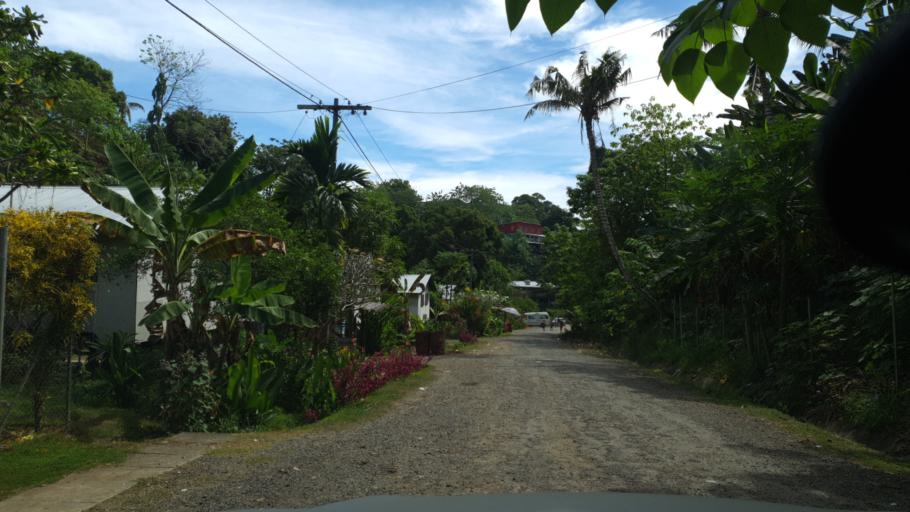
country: SB
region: Guadalcanal
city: Honiara
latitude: -9.4308
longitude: 159.9325
